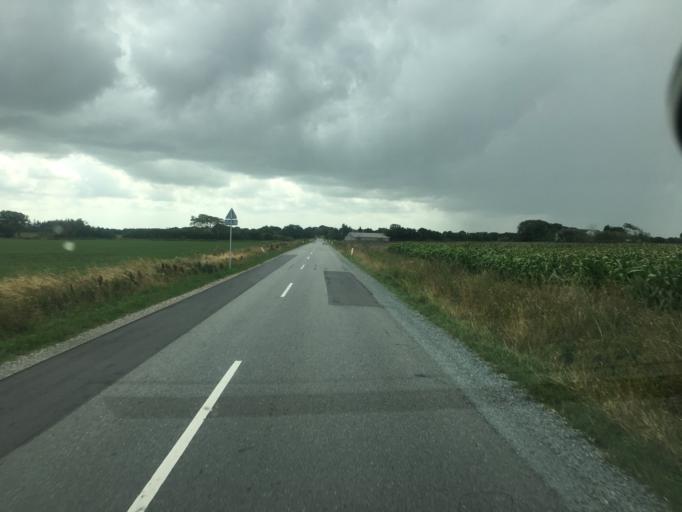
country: DK
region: South Denmark
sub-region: Tonder Kommune
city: Logumkloster
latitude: 55.0073
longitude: 8.9674
